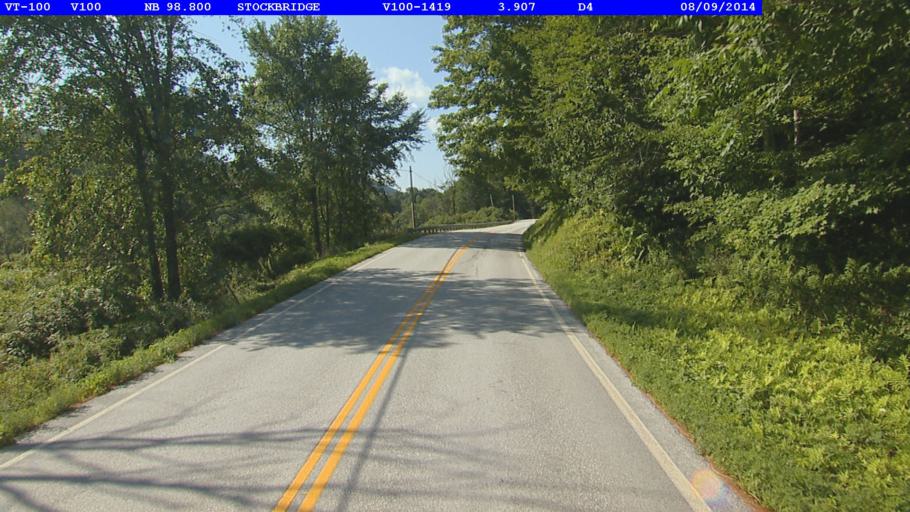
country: US
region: Vermont
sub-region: Orange County
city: Randolph
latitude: 43.7940
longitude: -72.7656
